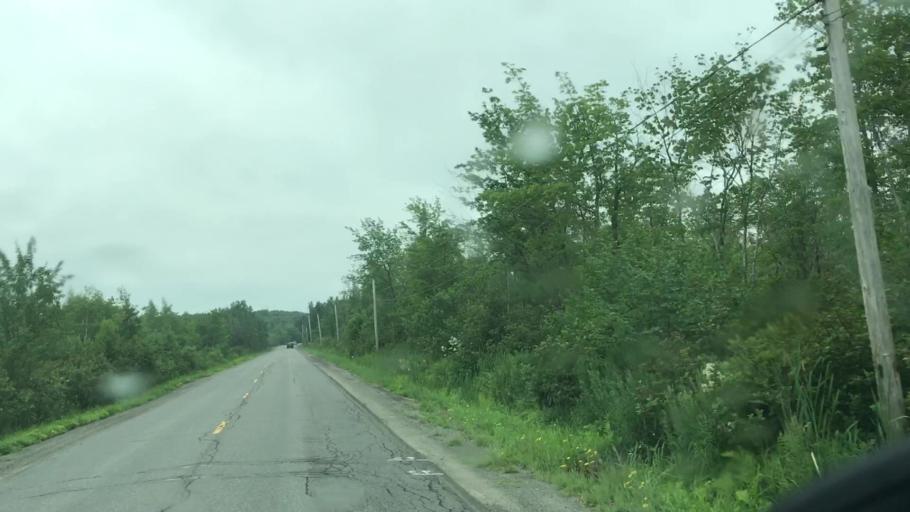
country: US
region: Maine
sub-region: Penobscot County
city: Veazie
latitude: 44.8709
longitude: -68.7151
